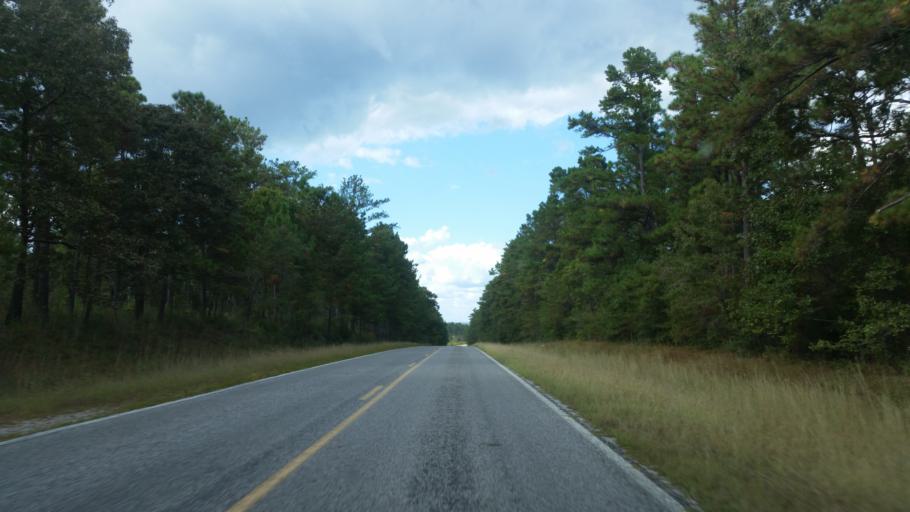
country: US
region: Mississippi
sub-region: Stone County
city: Wiggins
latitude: 30.9512
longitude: -89.0534
